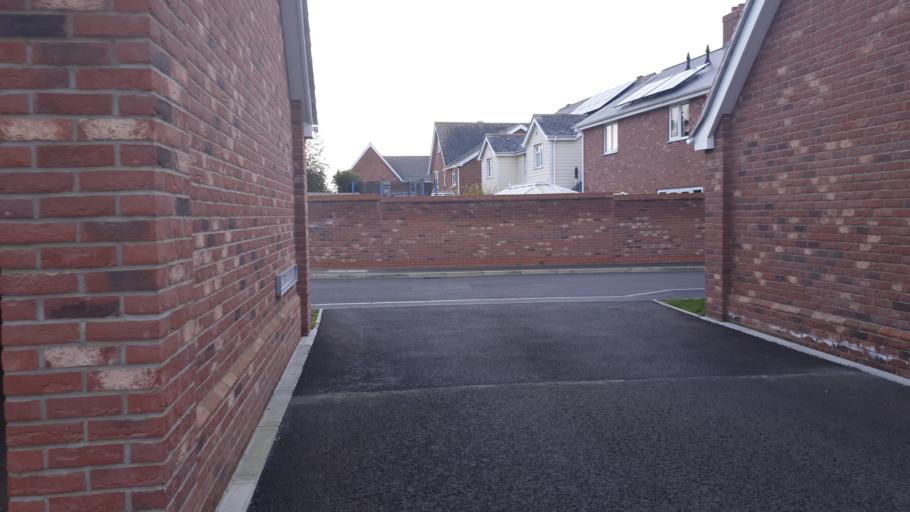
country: GB
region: England
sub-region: Essex
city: Little Clacton
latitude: 51.8365
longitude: 1.1364
